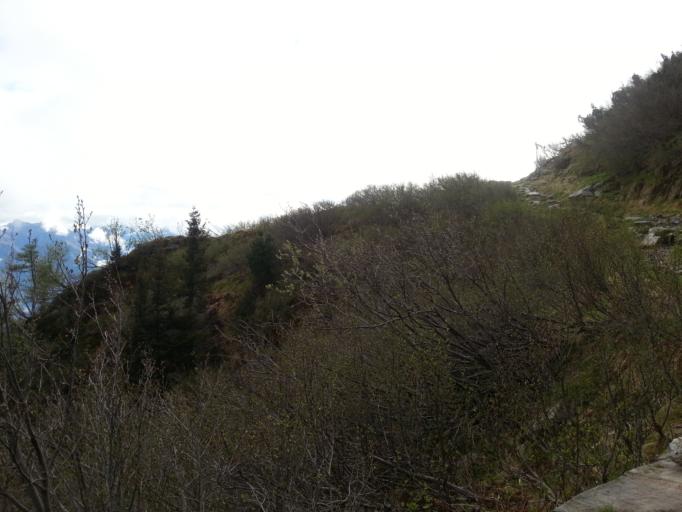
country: CH
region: Ticino
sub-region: Locarno District
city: Magadino
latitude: 46.1050
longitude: 8.8645
